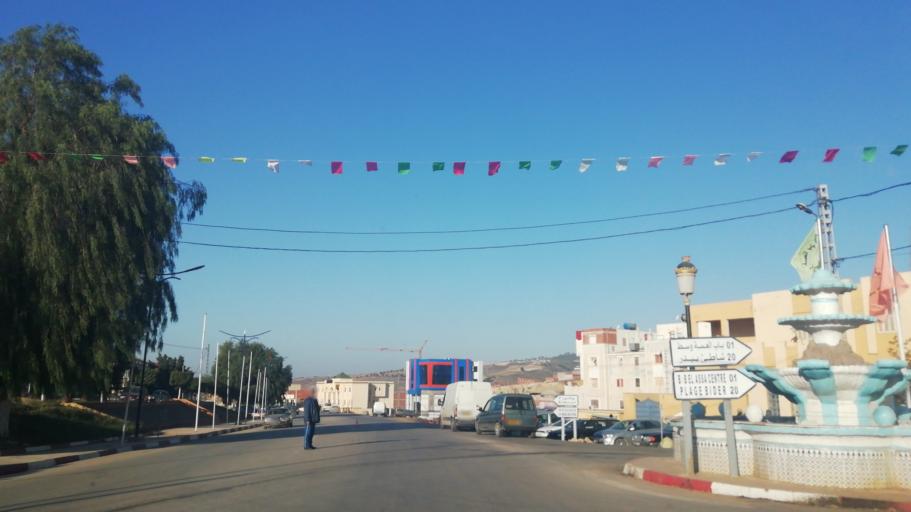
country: MA
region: Oriental
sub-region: Berkane-Taourirt
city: Ahfir
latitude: 34.9614
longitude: -2.0310
